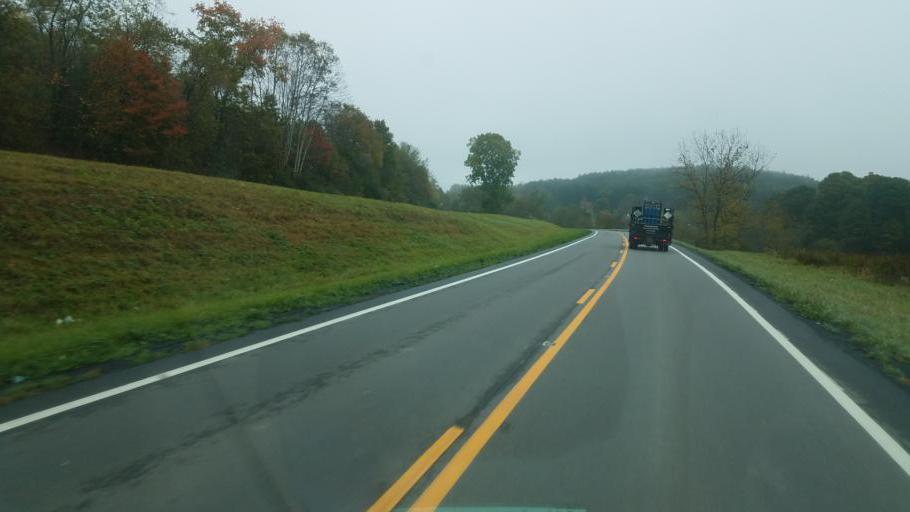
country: US
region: Ohio
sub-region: Tuscarawas County
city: Rockford
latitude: 40.4249
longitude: -81.2033
